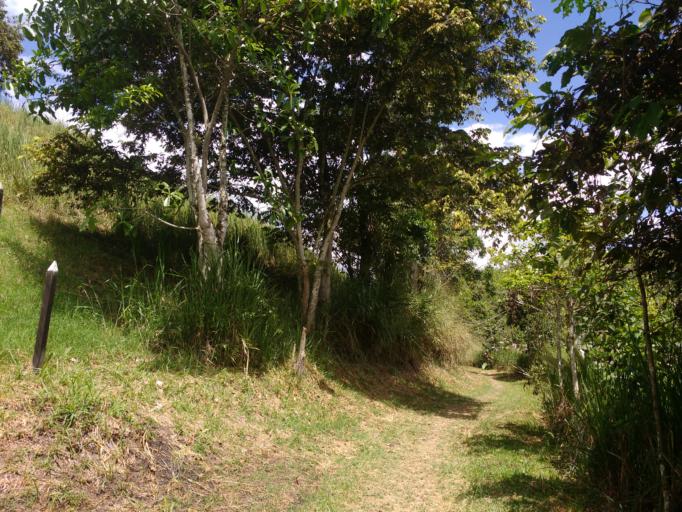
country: CO
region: Valle del Cauca
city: Alcala
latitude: 4.6763
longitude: -75.8112
